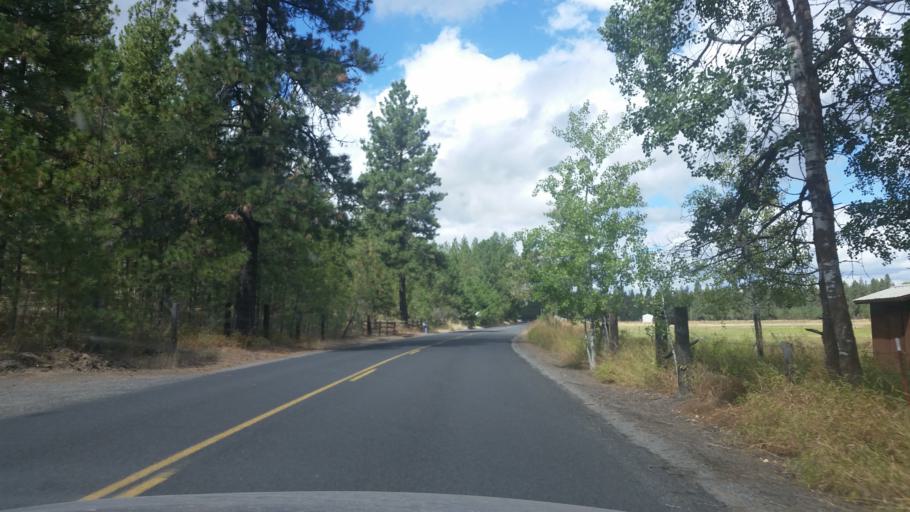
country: US
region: Washington
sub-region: Spokane County
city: Cheney
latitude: 47.5391
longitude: -117.4759
